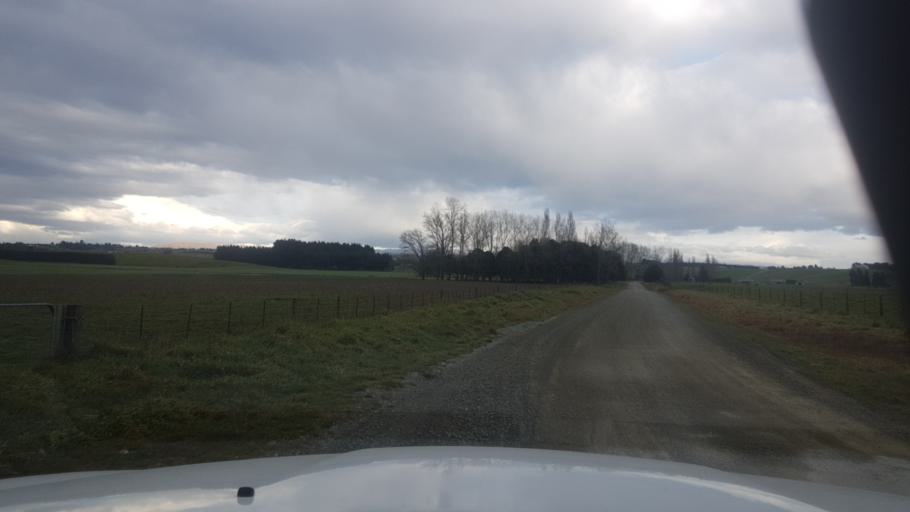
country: NZ
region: Canterbury
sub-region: Timaru District
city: Timaru
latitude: -44.3391
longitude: 171.1942
